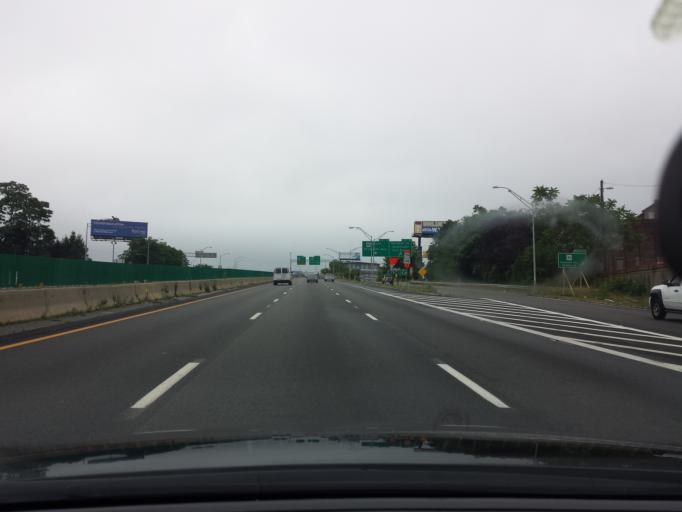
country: US
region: Massachusetts
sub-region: Bristol County
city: Fall River
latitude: 41.6992
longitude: -71.1529
